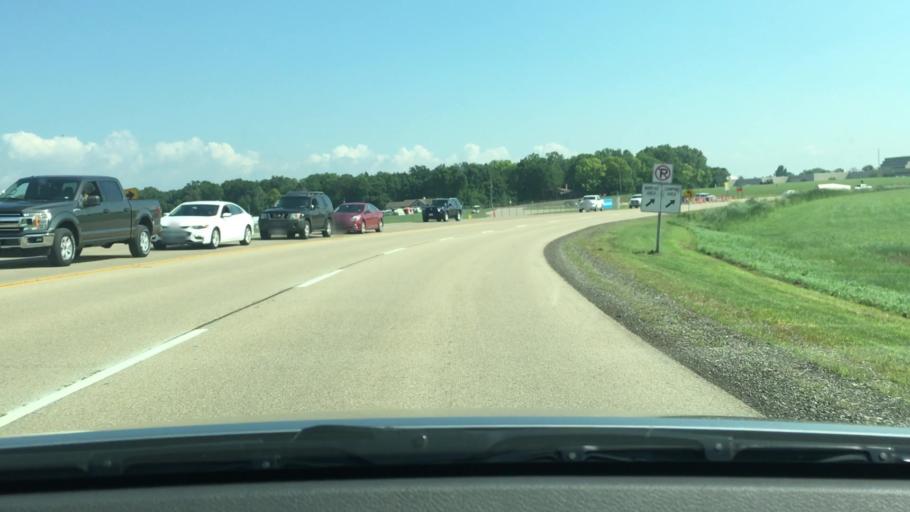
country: US
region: Wisconsin
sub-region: Winnebago County
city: Oshkosh
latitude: 43.9919
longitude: -88.5780
